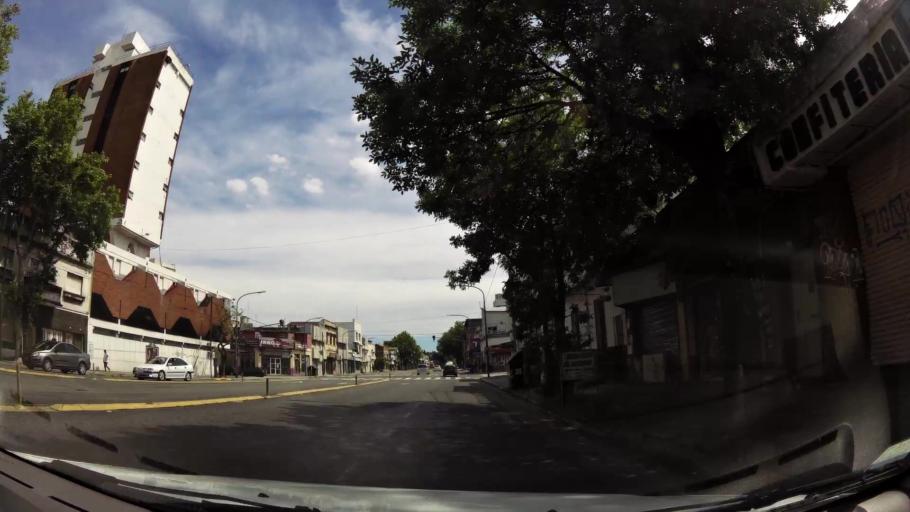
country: AR
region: Buenos Aires F.D.
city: Villa Santa Rita
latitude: -34.6226
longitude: -58.4816
